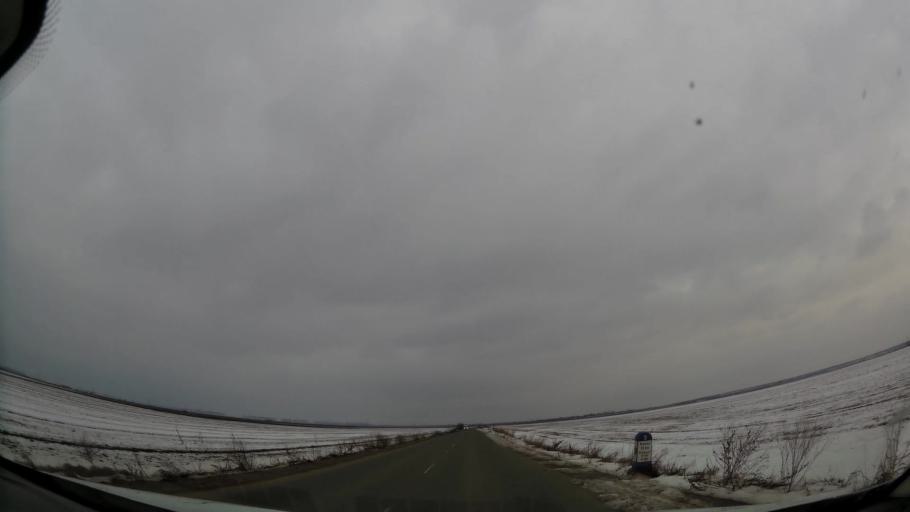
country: RO
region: Ilfov
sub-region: Comuna Tunari
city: Tunari
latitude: 44.5526
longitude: 26.1730
